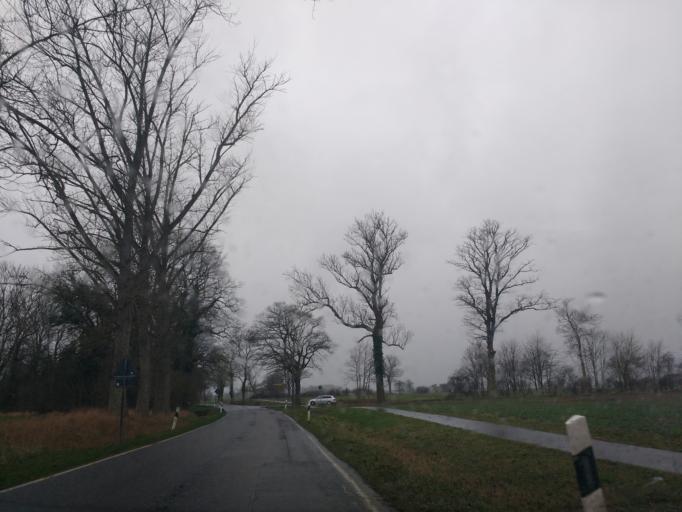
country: DE
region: Schleswig-Holstein
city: Gremersdorf
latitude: 54.3150
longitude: 10.9567
